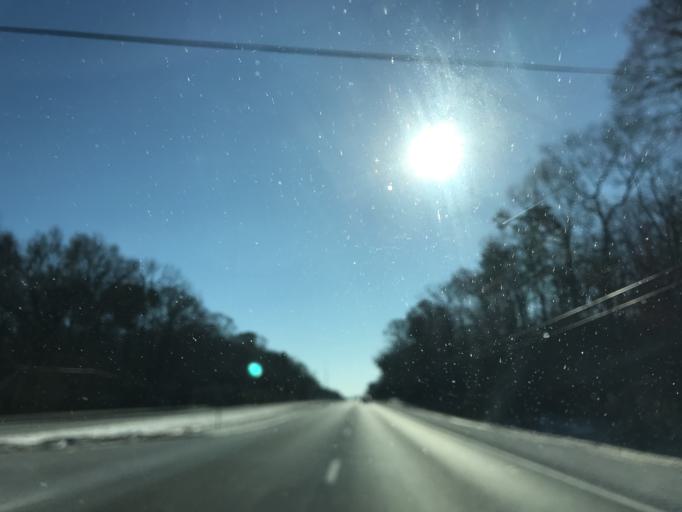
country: US
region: Maryland
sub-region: Charles County
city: La Plata
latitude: 38.4246
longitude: -76.9666
